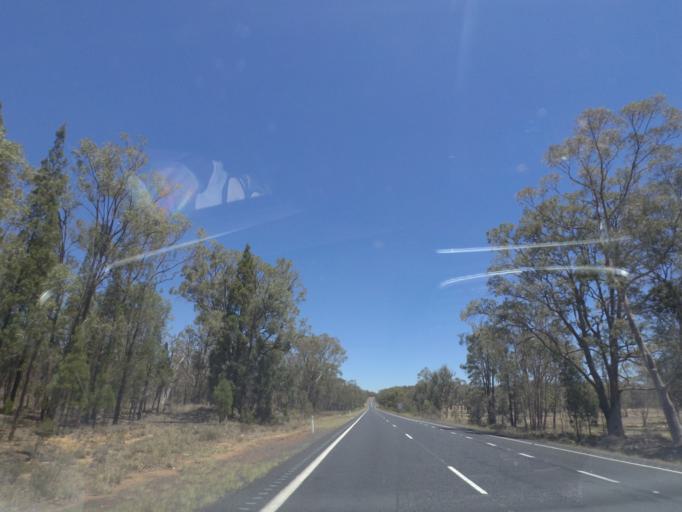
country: AU
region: New South Wales
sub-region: Warrumbungle Shire
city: Coonabarabran
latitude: -31.2212
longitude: 149.3248
